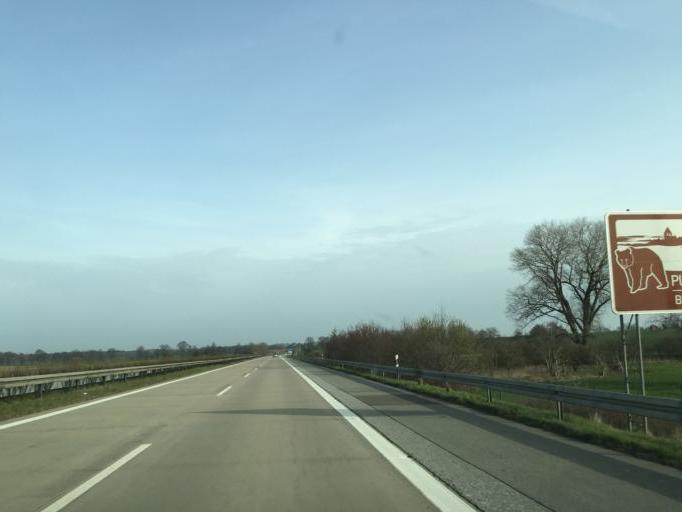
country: DE
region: Mecklenburg-Vorpommern
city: Robel
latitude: 53.3392
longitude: 12.4754
